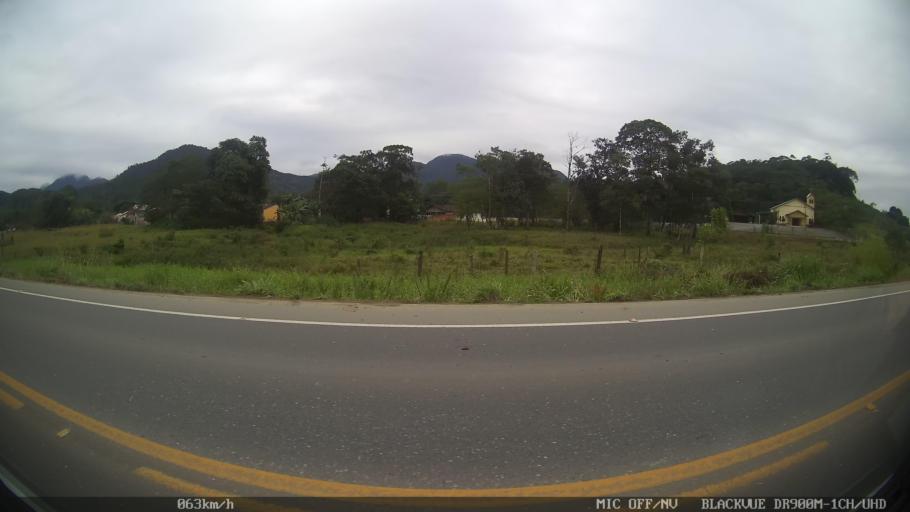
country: BR
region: Santa Catarina
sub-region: Joinville
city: Joinville
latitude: -26.2667
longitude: -48.9210
